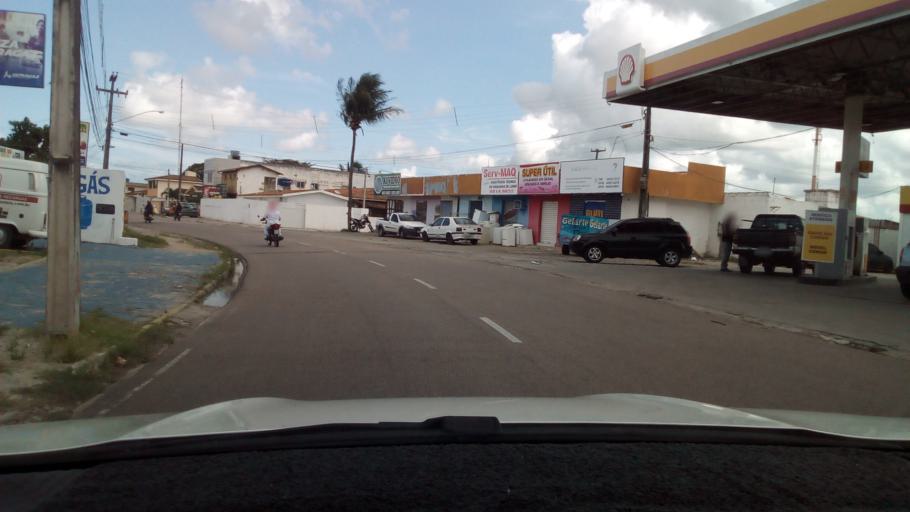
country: BR
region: Paraiba
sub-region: Joao Pessoa
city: Joao Pessoa
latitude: -7.1520
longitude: -34.8749
